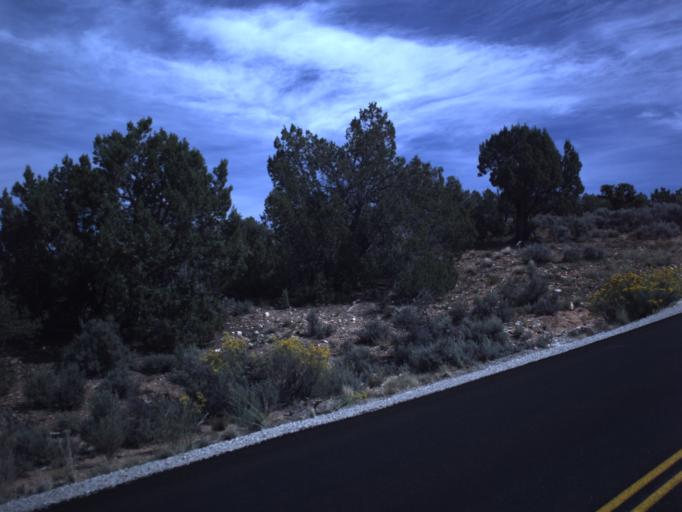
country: US
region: Utah
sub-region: San Juan County
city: Blanding
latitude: 37.5743
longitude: -109.5494
